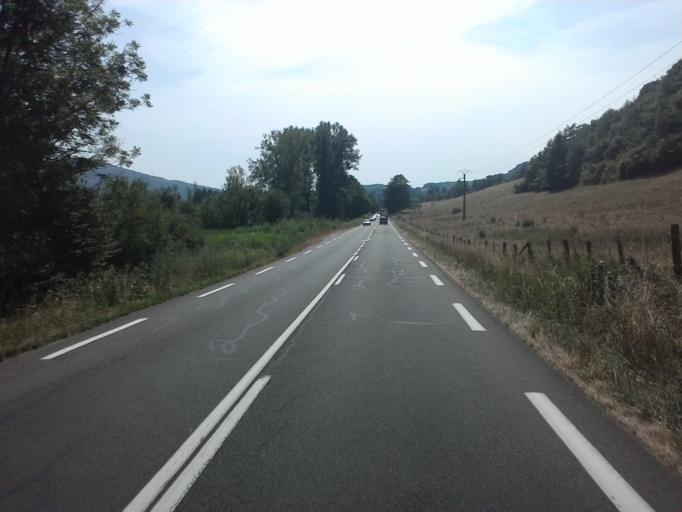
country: FR
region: Rhone-Alpes
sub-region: Departement de l'Isere
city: Chirens
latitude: 45.4228
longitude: 5.5576
